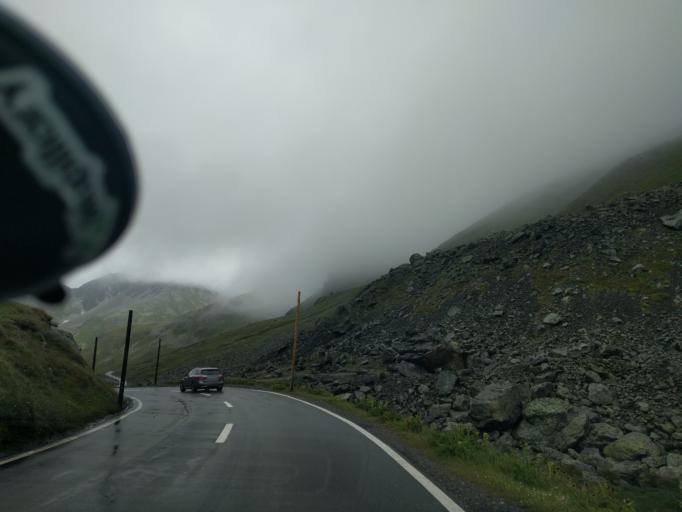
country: CH
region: Grisons
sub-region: Praettigau/Davos District
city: Davos
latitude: 46.7471
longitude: 9.9509
